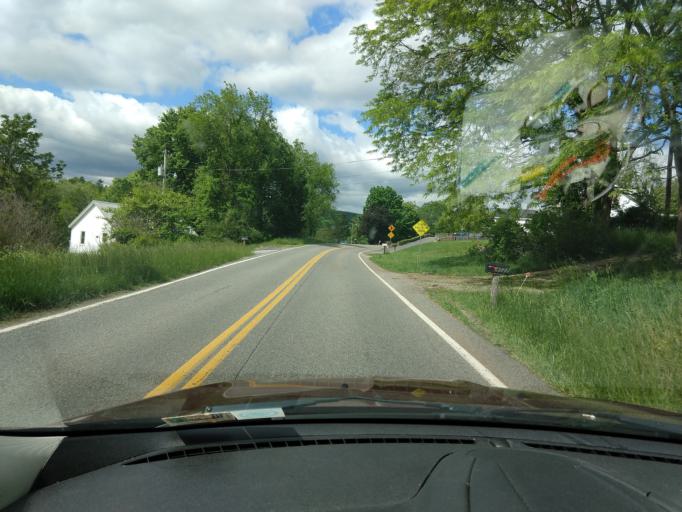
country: US
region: Virginia
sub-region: Wythe County
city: Wytheville
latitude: 36.8380
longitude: -80.9584
